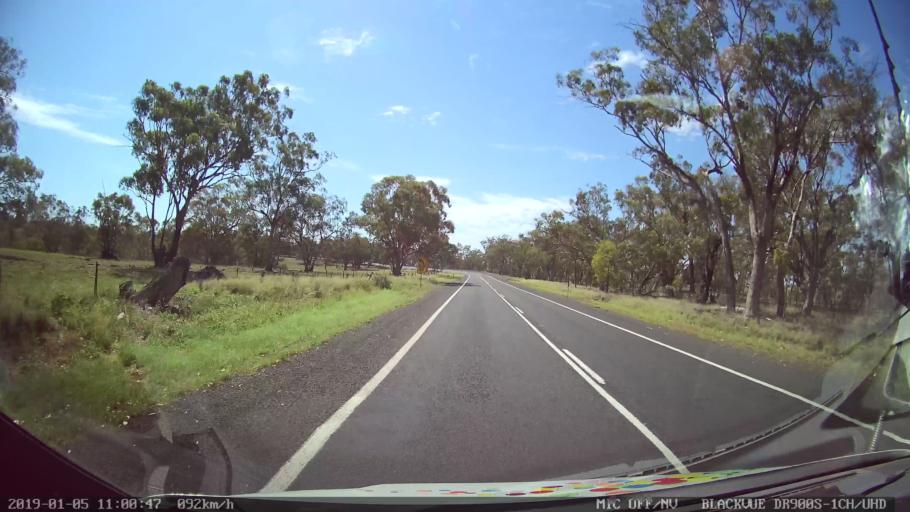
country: AU
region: New South Wales
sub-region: Warrumbungle Shire
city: Coonabarabran
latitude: -31.4210
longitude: 149.2161
